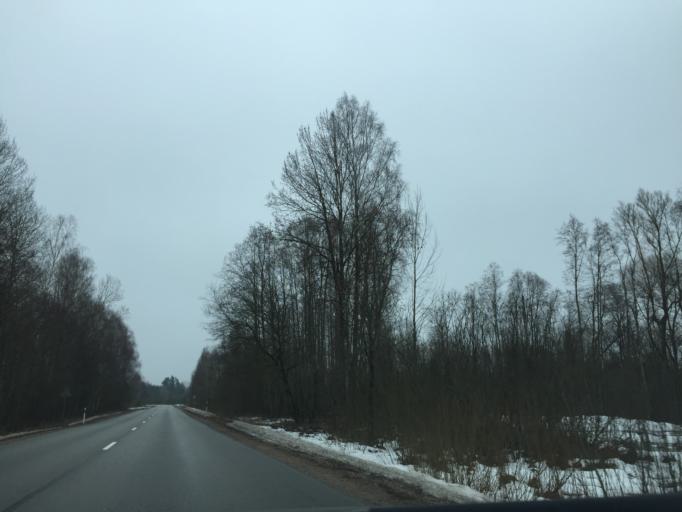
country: LV
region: Lecava
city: Iecava
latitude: 56.6088
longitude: 24.0399
